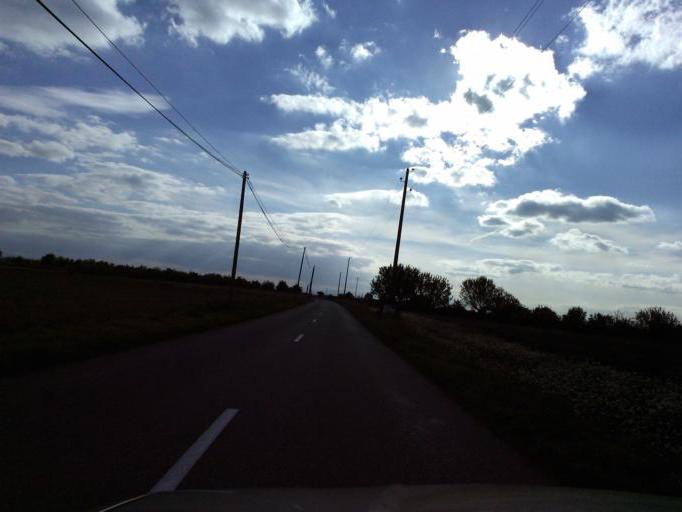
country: FR
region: Provence-Alpes-Cote d'Azur
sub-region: Departement des Alpes-de-Haute-Provence
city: Valensole
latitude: 43.8522
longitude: 5.9948
